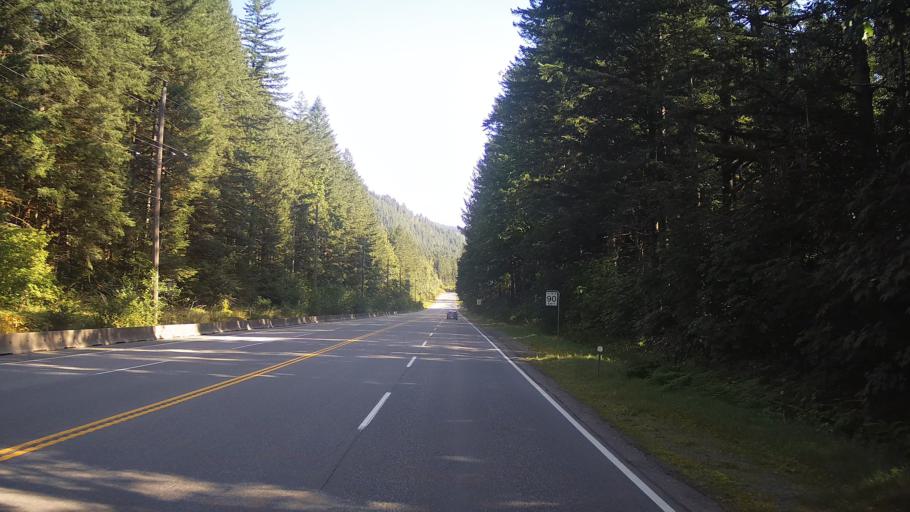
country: CA
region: British Columbia
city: Hope
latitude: 49.4532
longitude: -121.4368
